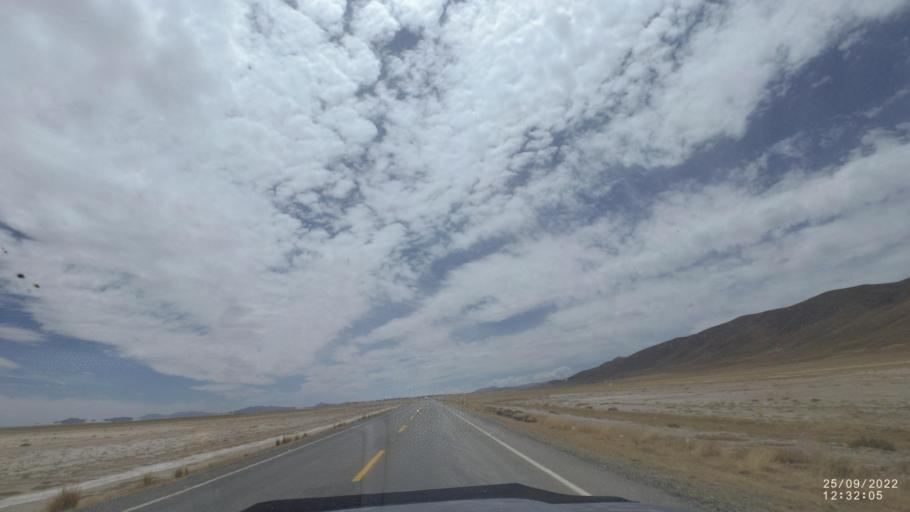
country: BO
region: Oruro
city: Machacamarca
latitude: -18.2188
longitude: -67.0081
